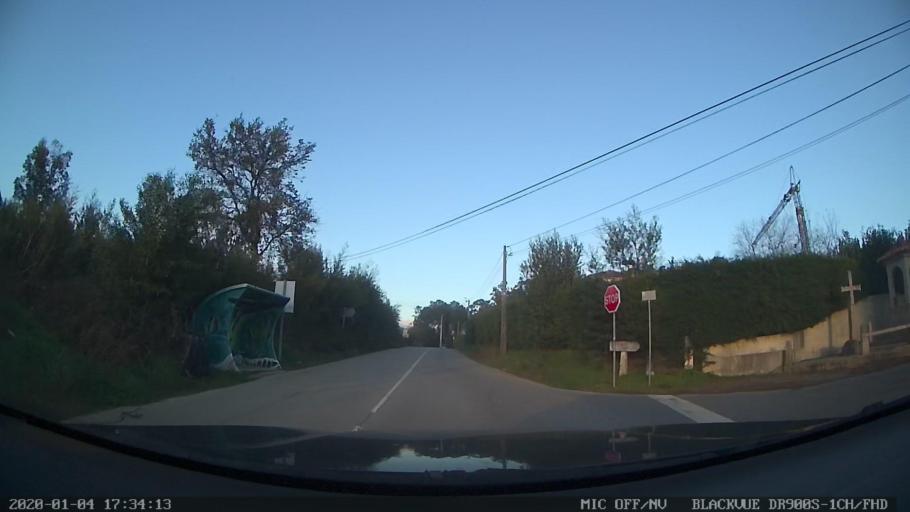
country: PT
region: Vila Real
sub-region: Mondim de Basto
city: Mondim de Basto
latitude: 41.4364
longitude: -7.9723
